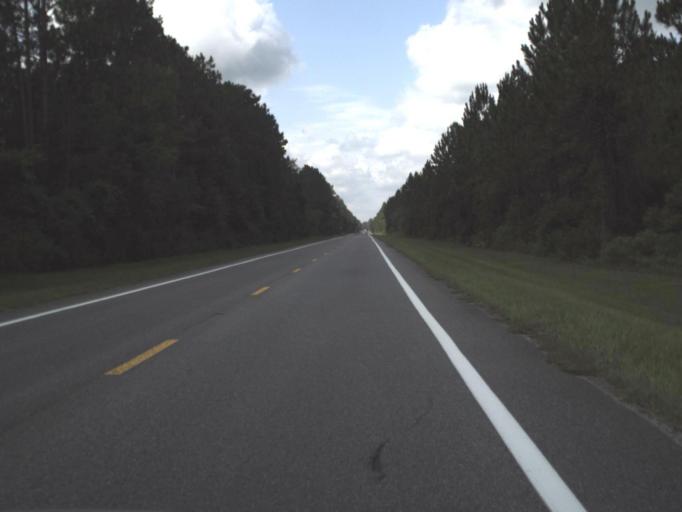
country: US
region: Florida
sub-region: Baker County
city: Macclenny
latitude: 30.1316
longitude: -82.1976
